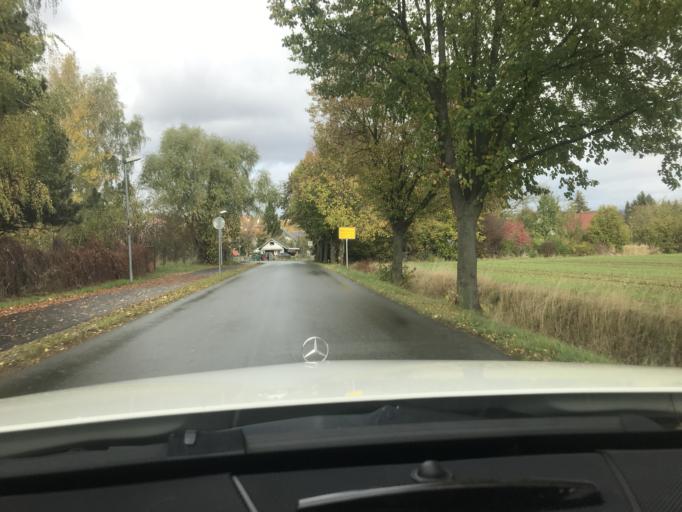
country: DE
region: Thuringia
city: Oberdorla
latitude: 51.1595
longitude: 10.4203
